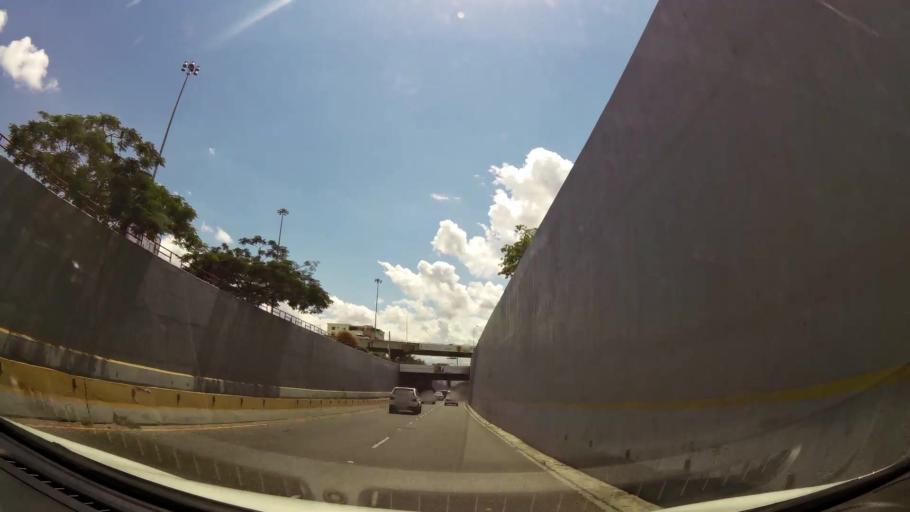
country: DO
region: Santiago
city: Santiago de los Caballeros
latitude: 19.4509
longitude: -70.6860
